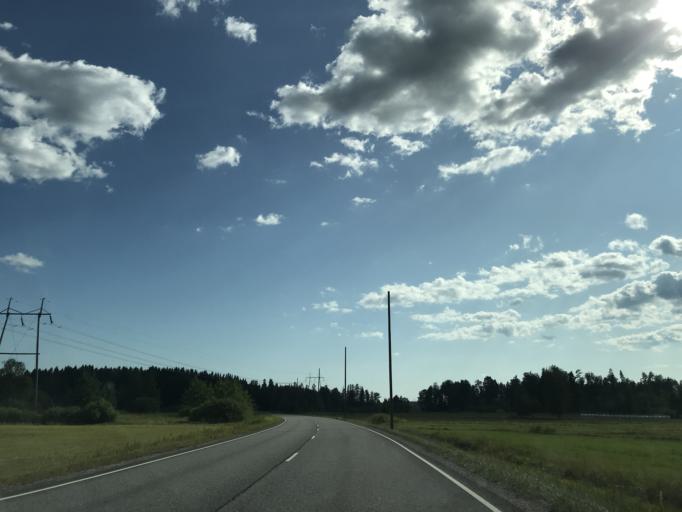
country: FI
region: Uusimaa
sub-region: Helsinki
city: Nurmijaervi
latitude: 60.4534
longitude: 24.7040
